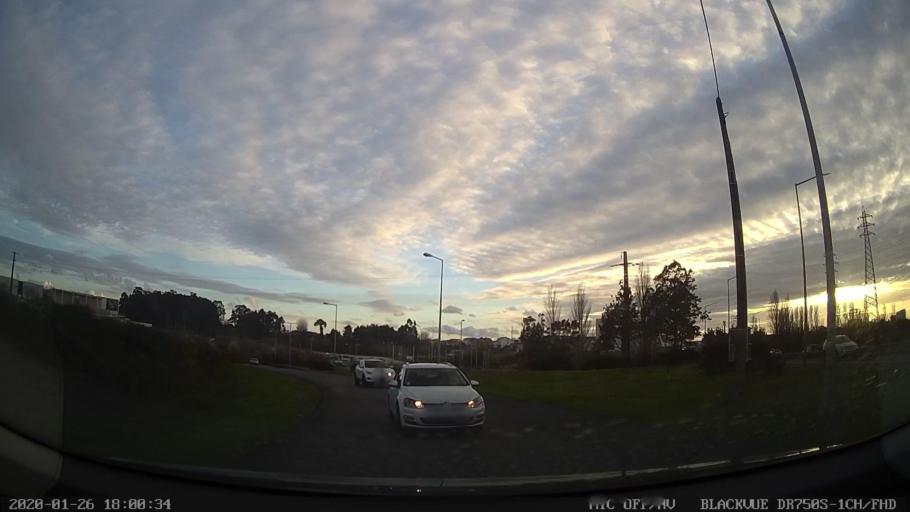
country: PT
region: Aveiro
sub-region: Aveiro
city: Aveiro
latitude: 40.6369
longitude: -8.6345
